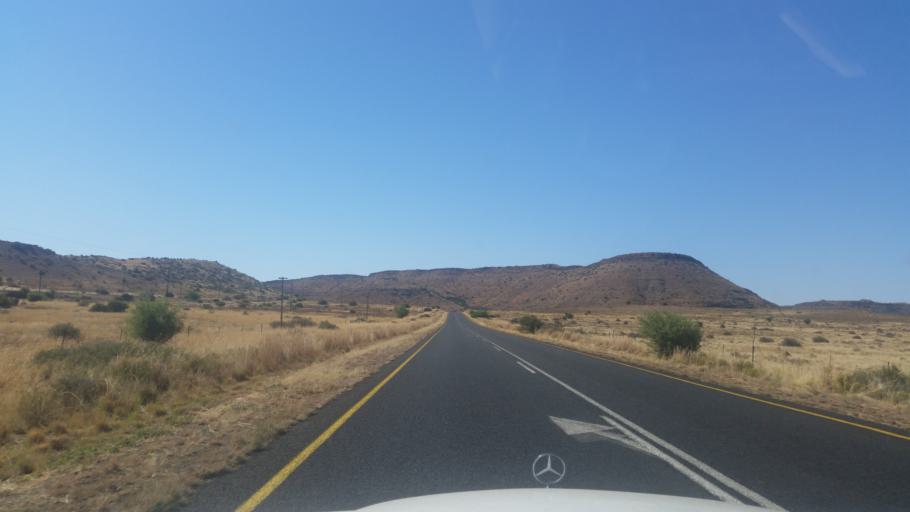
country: ZA
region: Orange Free State
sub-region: Xhariep District Municipality
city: Trompsburg
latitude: -30.5071
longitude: 26.0169
